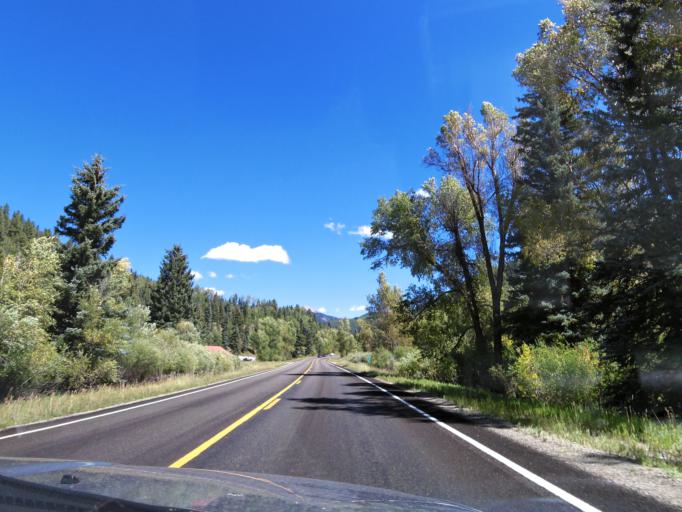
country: US
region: Colorado
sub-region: Montezuma County
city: Mancos
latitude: 37.6093
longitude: -108.0912
